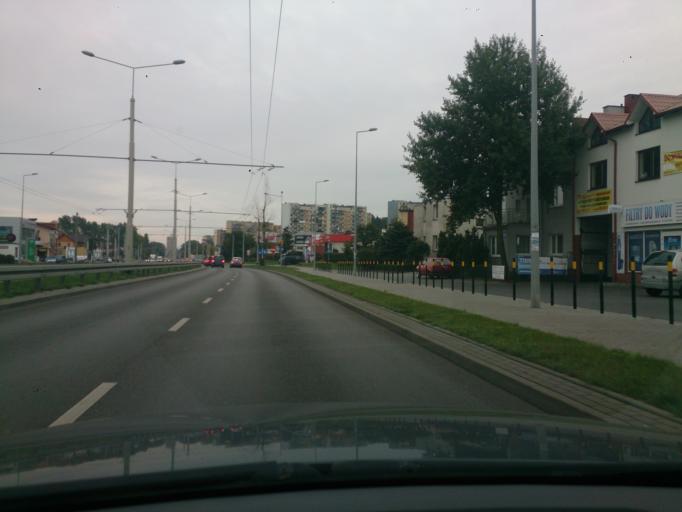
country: PL
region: Pomeranian Voivodeship
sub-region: Gdynia
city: Pogorze
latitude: 54.5473
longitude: 18.4371
